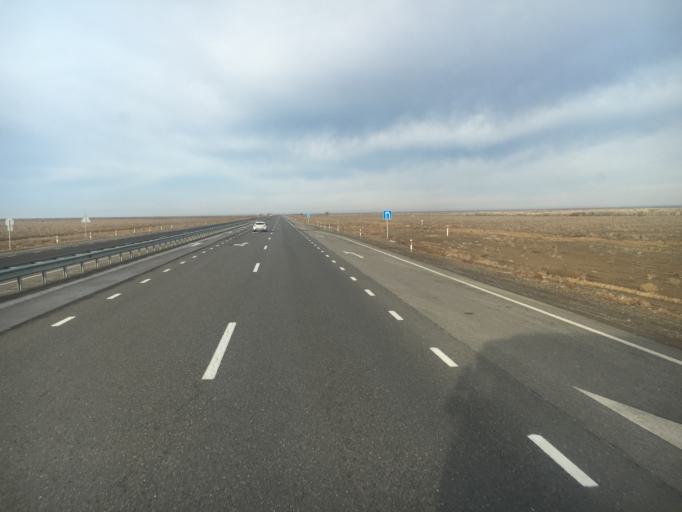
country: KZ
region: Ongtustik Qazaqstan
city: Turkestan
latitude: 43.5176
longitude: 67.8108
